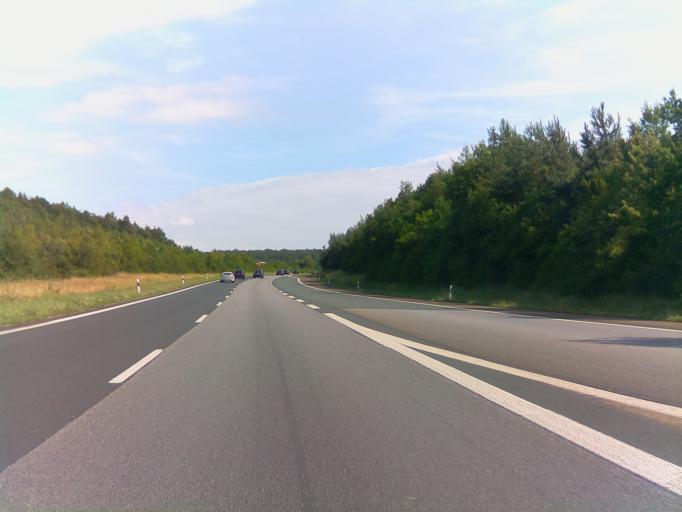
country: DE
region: Bavaria
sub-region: Regierungsbezirk Unterfranken
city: Eisingen
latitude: 49.7430
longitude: 9.8193
